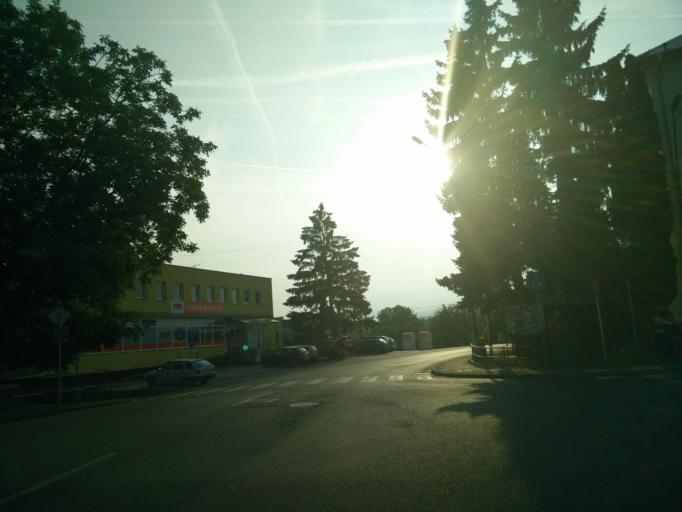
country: SK
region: Nitriansky
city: Banovce nad Bebravou
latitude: 48.7876
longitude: 18.1637
